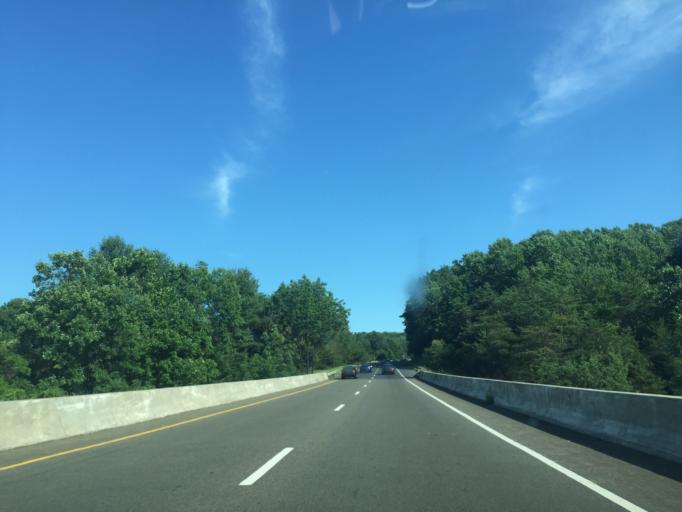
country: US
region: Maryland
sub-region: Baltimore County
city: Hunt Valley
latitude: 39.6133
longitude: -76.6615
